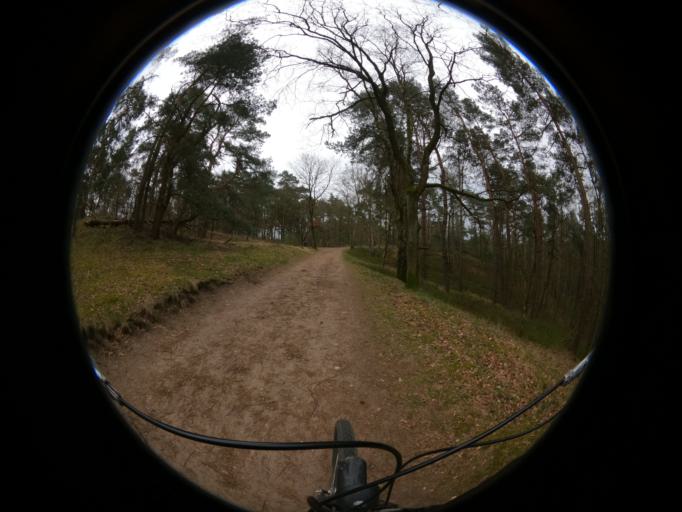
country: DE
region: Lower Saxony
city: Neu Wulmstorf
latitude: 53.4615
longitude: 9.8485
